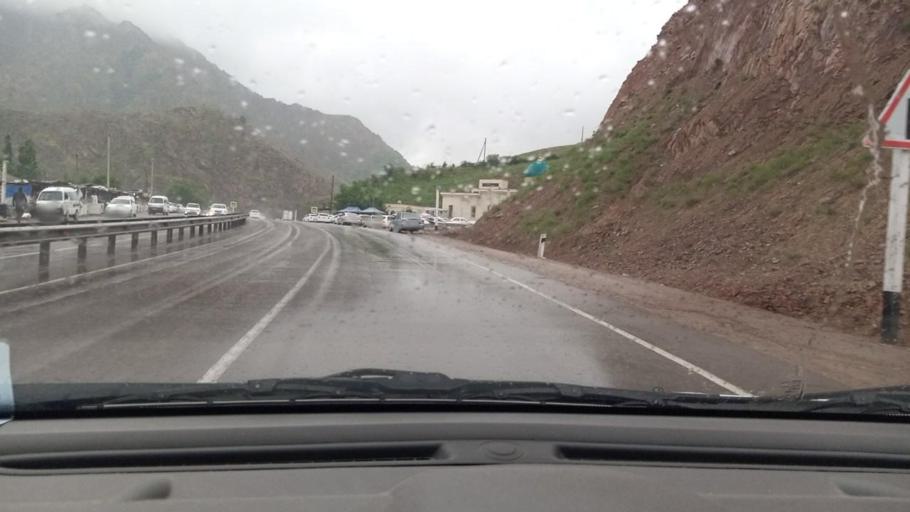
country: UZ
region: Toshkent
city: Angren
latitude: 41.1073
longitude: 70.3346
